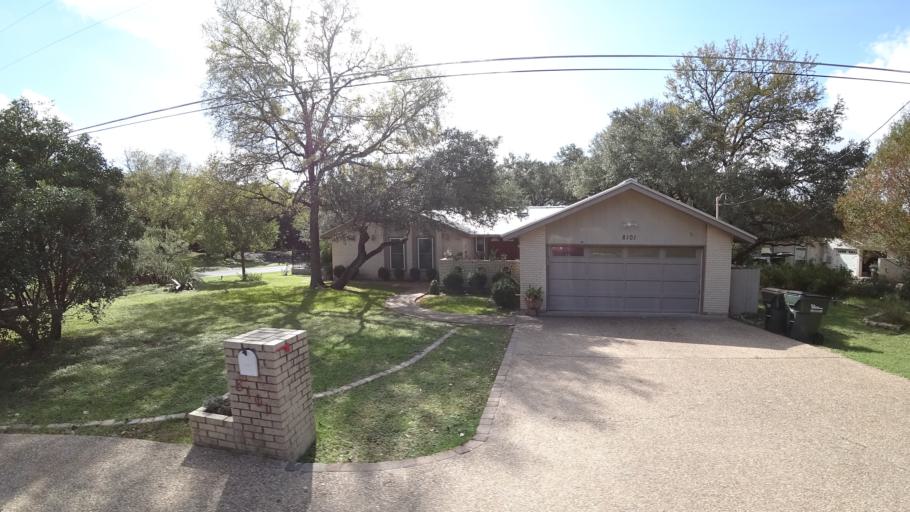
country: US
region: Texas
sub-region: Williamson County
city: Jollyville
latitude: 30.4210
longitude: -97.7830
